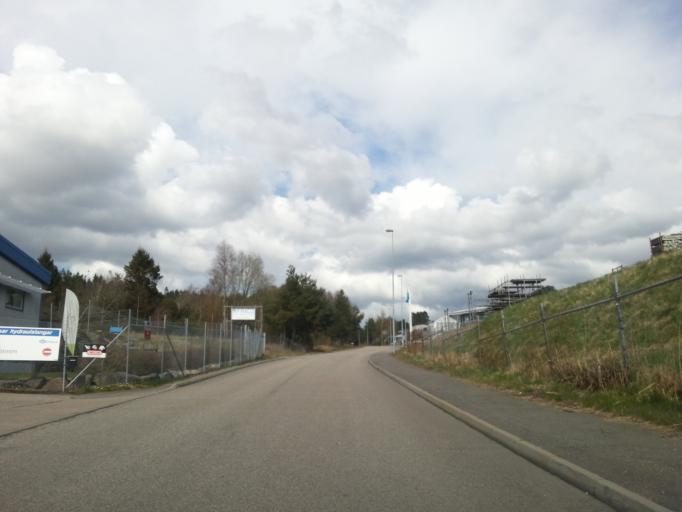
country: SE
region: Vaestra Goetaland
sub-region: Kungalvs Kommun
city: Kungalv
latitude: 57.8781
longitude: 11.9282
